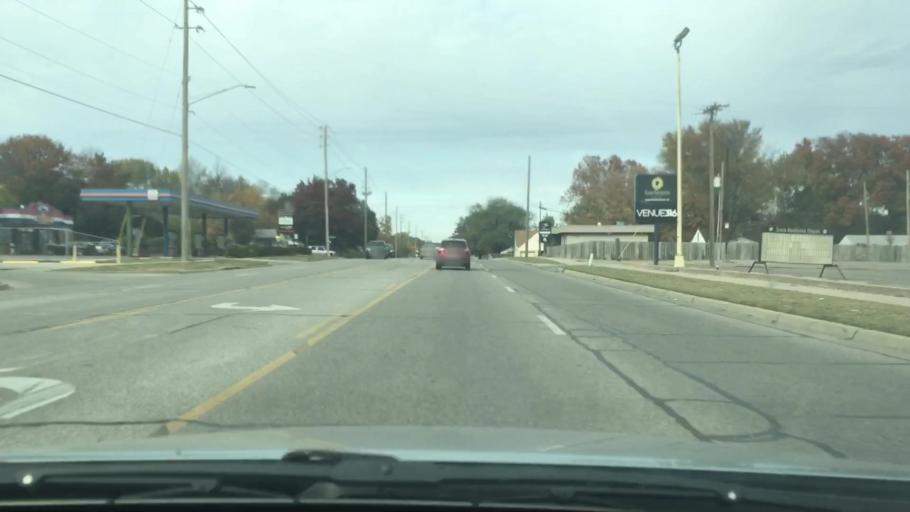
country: US
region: Kansas
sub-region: Sedgwick County
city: Wichita
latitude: 37.6727
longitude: -97.2804
